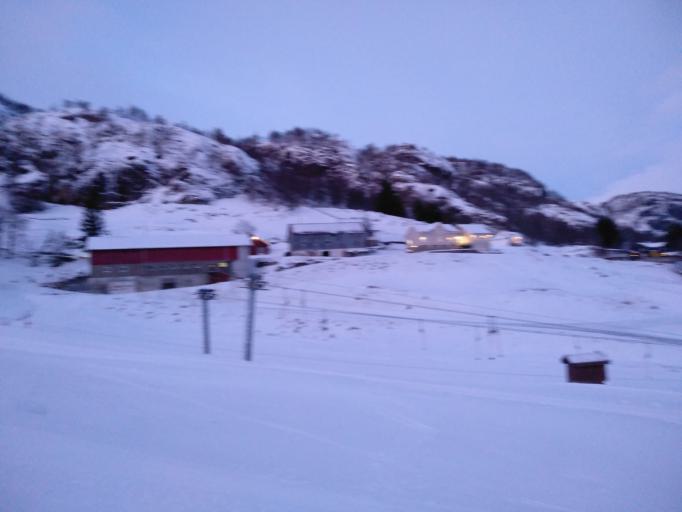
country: NO
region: Vest-Agder
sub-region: Sirdal
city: Tonstad
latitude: 59.0218
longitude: 6.9219
